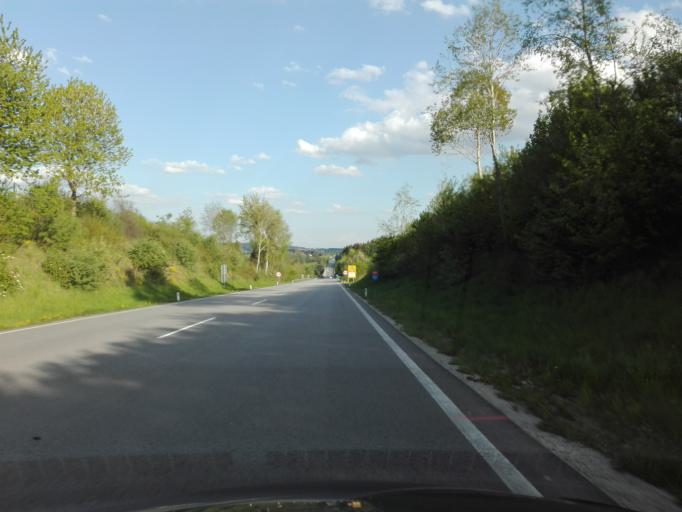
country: AT
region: Upper Austria
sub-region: Politischer Bezirk Rohrbach
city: Kleinzell im Muehlkreis
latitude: 48.4813
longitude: 13.9865
